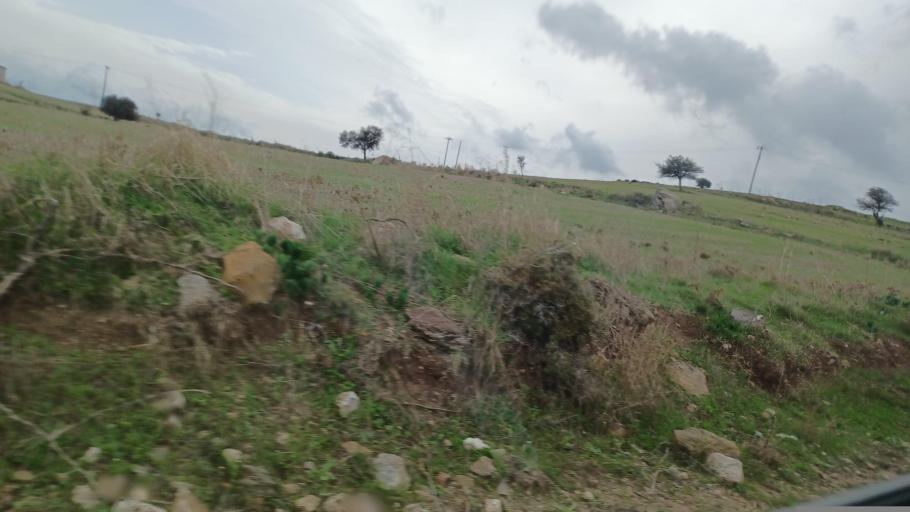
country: CY
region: Pafos
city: Polis
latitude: 34.9951
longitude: 32.3804
